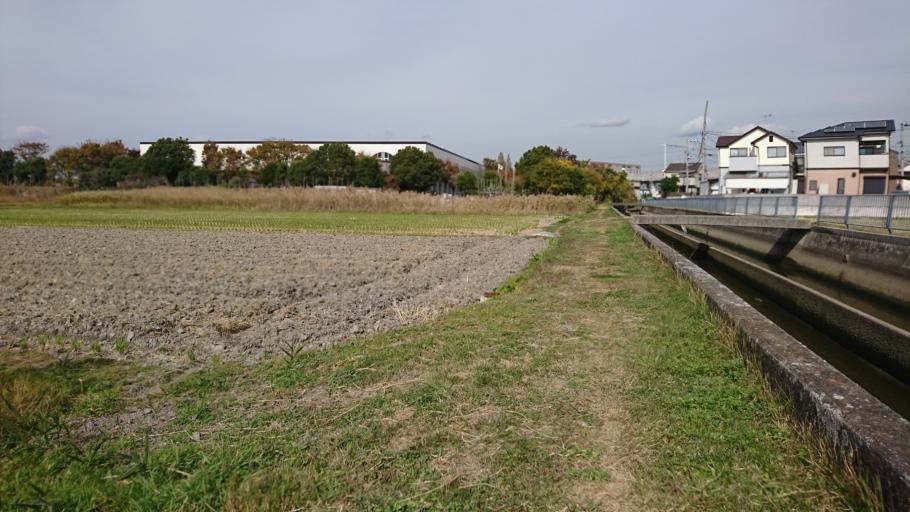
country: JP
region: Hyogo
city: Kakogawacho-honmachi
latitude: 34.7555
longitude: 134.8116
